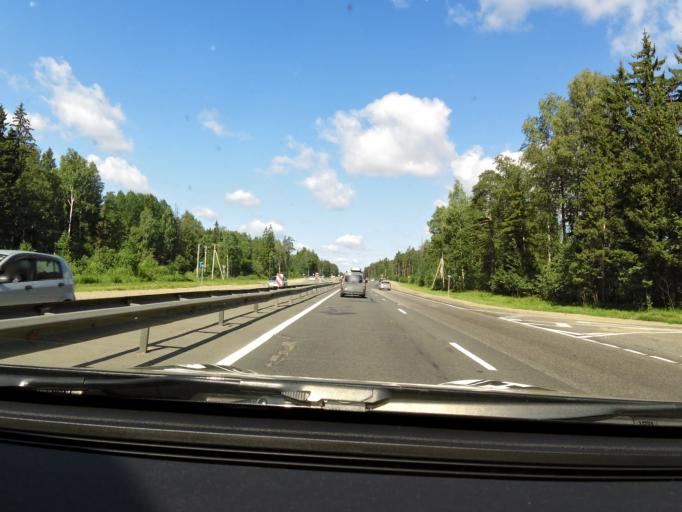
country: RU
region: Tverskaya
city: Tver
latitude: 56.8943
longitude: 35.7196
